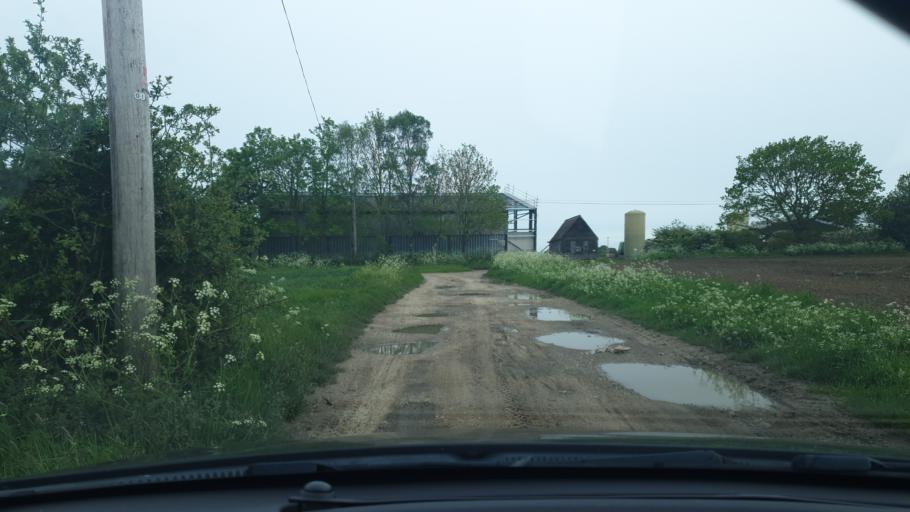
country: GB
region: England
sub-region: Essex
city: Mistley
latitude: 51.9068
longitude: 1.1147
